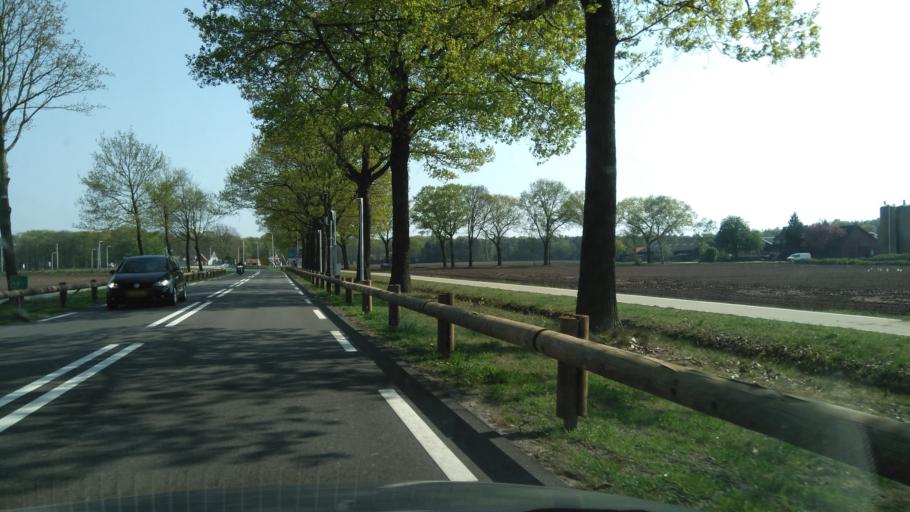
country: NL
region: North Brabant
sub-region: Gemeente Baarle-Nassau
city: Baarle-Nassau
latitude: 51.4602
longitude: 4.9115
